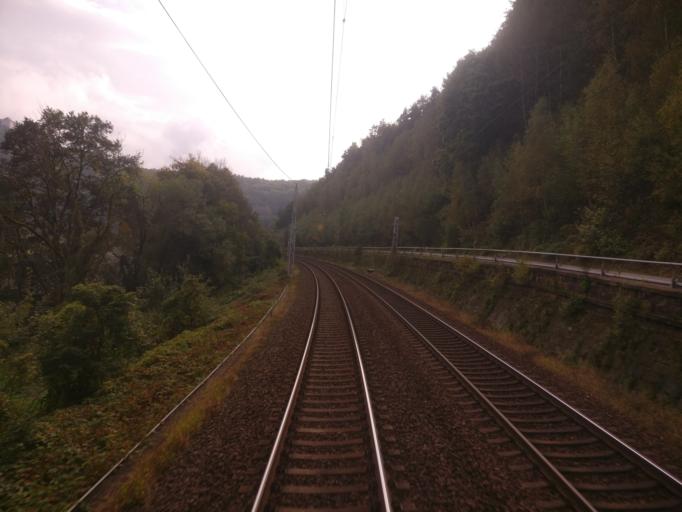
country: DE
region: Saxony
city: Konigstein
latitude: 50.9336
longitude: 14.0584
